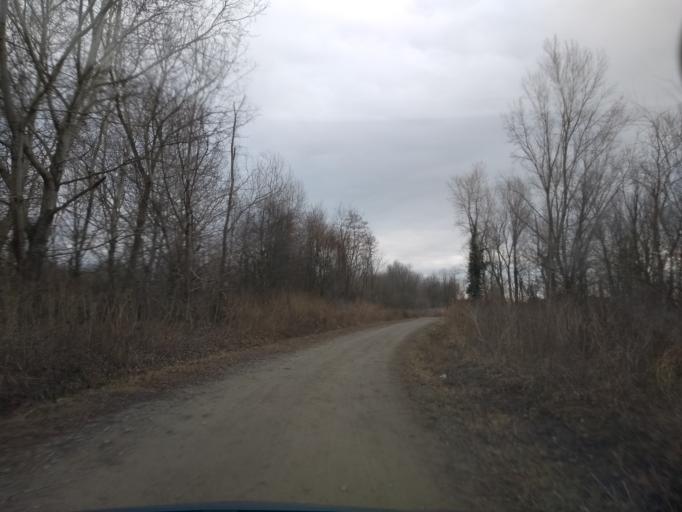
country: IT
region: Piedmont
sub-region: Provincia di Torino
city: Fiorano Canavese
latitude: 45.4893
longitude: 7.8388
